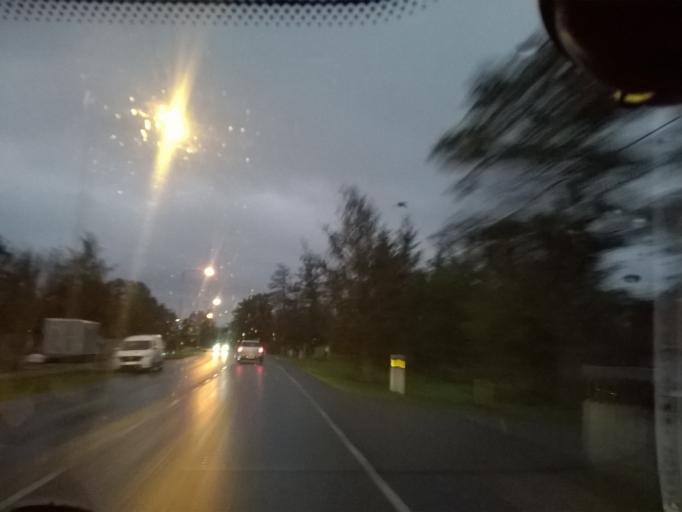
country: EE
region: Harju
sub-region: Viimsi vald
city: Rummu
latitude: 59.5415
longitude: 24.7950
